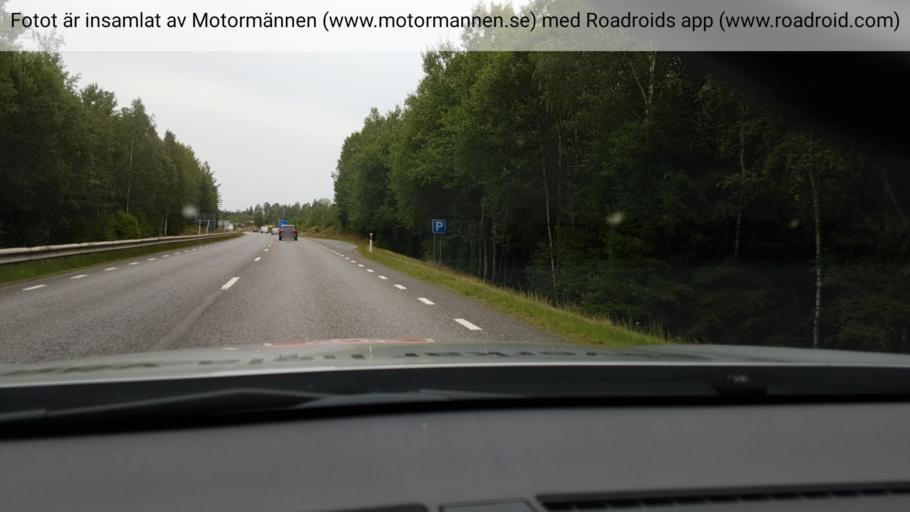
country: SE
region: Vaestra Goetaland
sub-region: Tranemo Kommun
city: Tranemo
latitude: 57.4858
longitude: 13.3688
